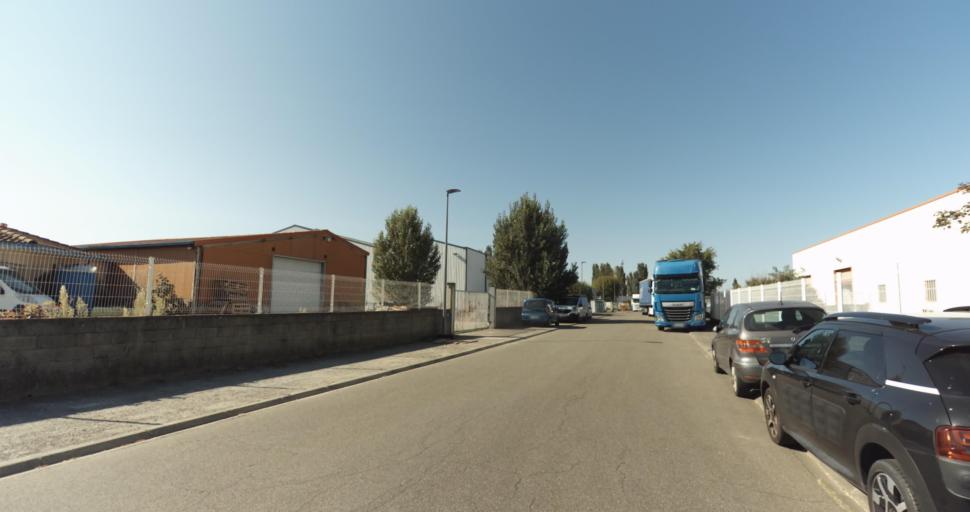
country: FR
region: Midi-Pyrenees
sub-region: Departement de la Haute-Garonne
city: Launaguet
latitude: 43.6626
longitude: 1.4621
